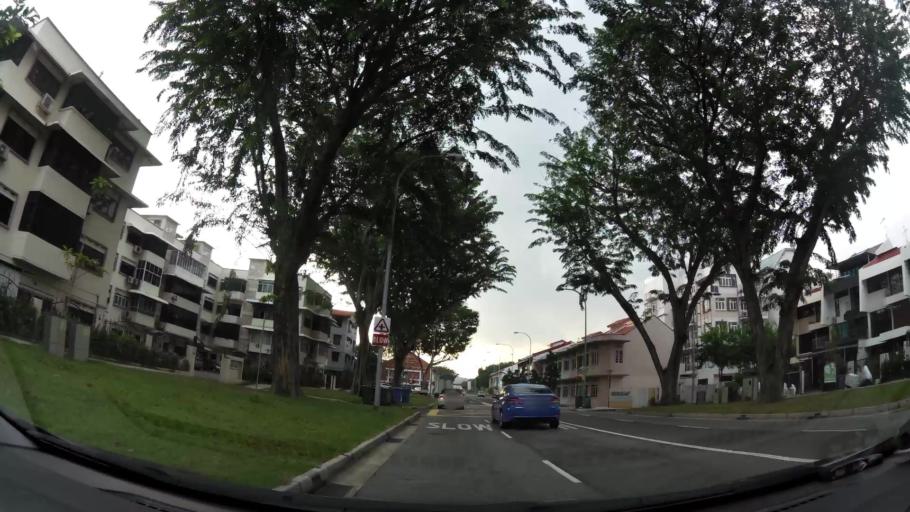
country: SG
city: Singapore
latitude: 1.3091
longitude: 103.9132
